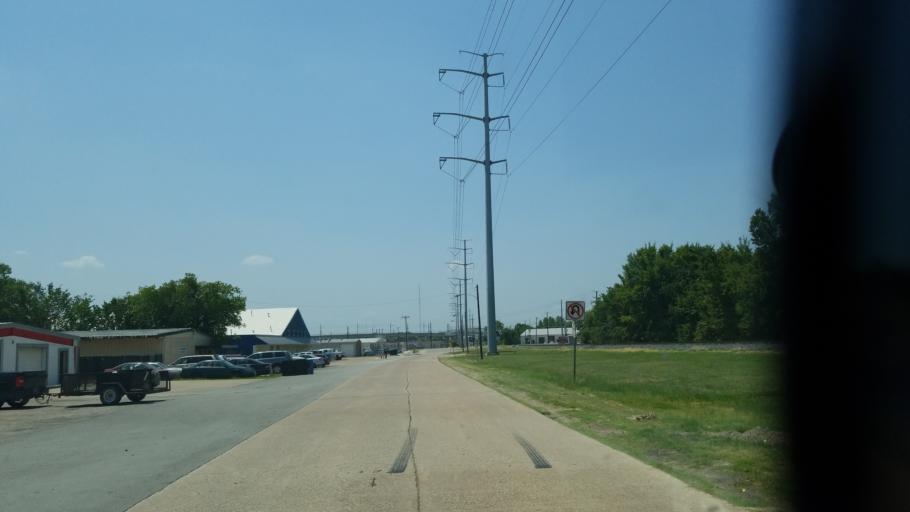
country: US
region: Texas
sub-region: Dallas County
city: Garland
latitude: 32.9210
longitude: -96.6293
